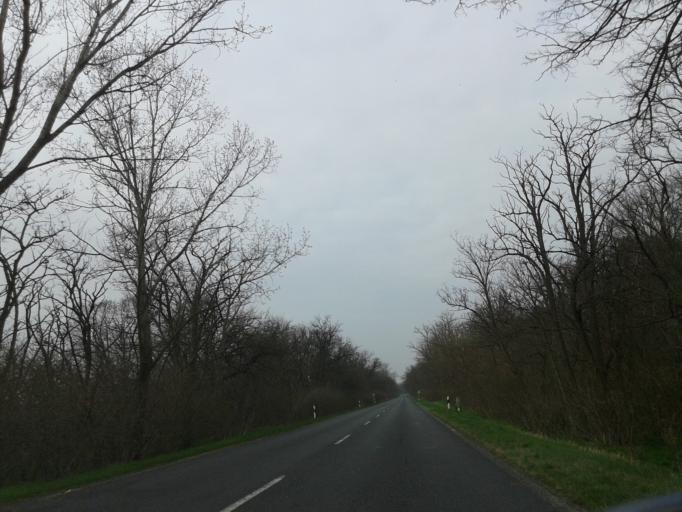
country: HU
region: Gyor-Moson-Sopron
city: Bony
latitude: 47.7358
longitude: 17.9160
